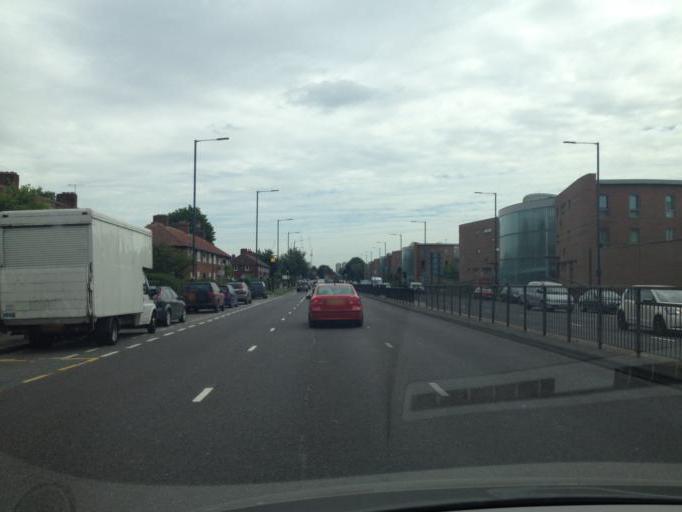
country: GB
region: England
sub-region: Greater London
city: Hammersmith
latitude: 51.5140
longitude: -0.2477
